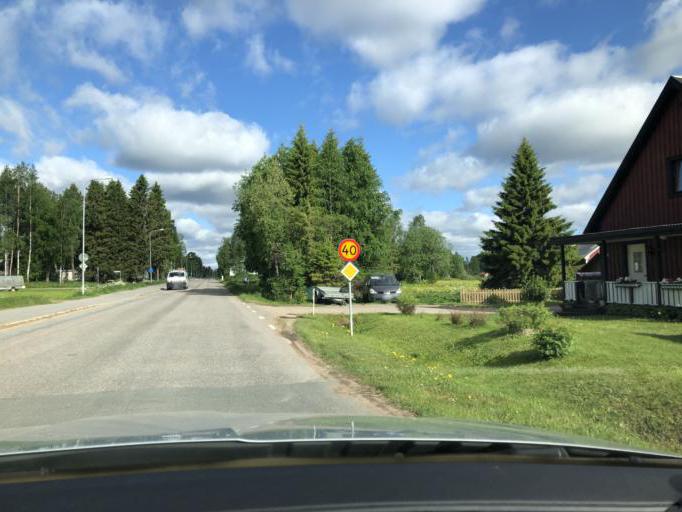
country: SE
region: Norrbotten
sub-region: Pajala Kommun
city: Pajala
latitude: 67.2189
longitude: 23.3541
